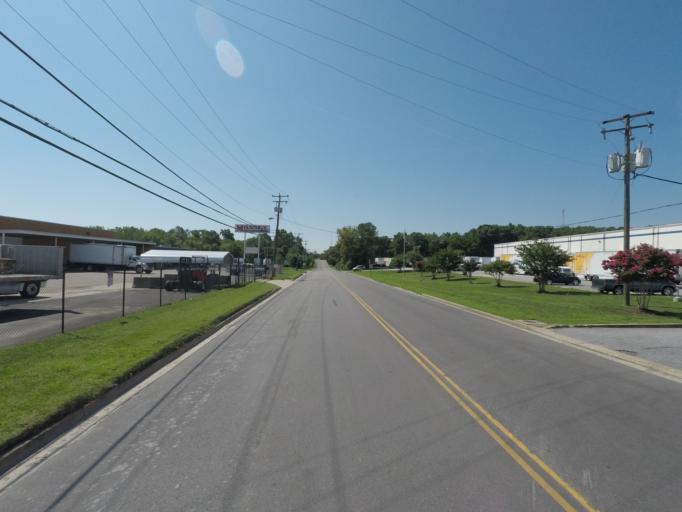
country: US
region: Virginia
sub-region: Henrico County
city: Dumbarton
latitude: 37.5910
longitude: -77.4858
